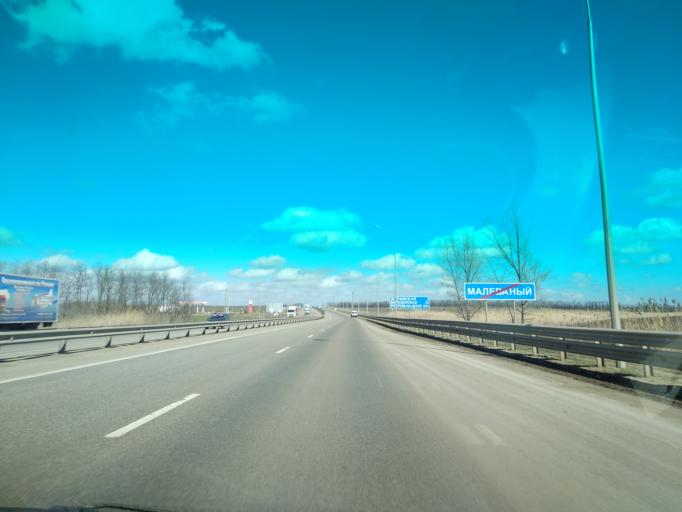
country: RU
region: Krasnodarskiy
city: Korenovsk
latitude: 45.5321
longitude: 39.4623
